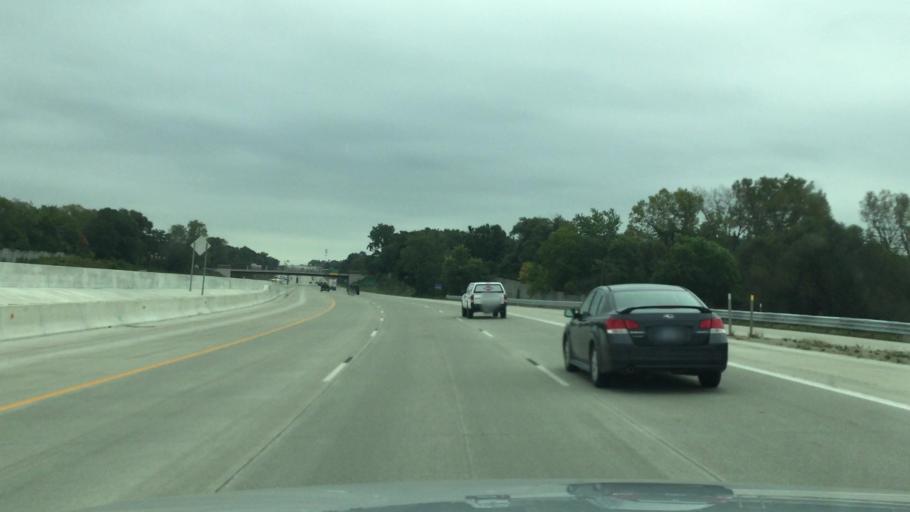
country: US
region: Michigan
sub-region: Oakland County
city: Bloomfield Hills
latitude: 42.6121
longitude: -83.2294
